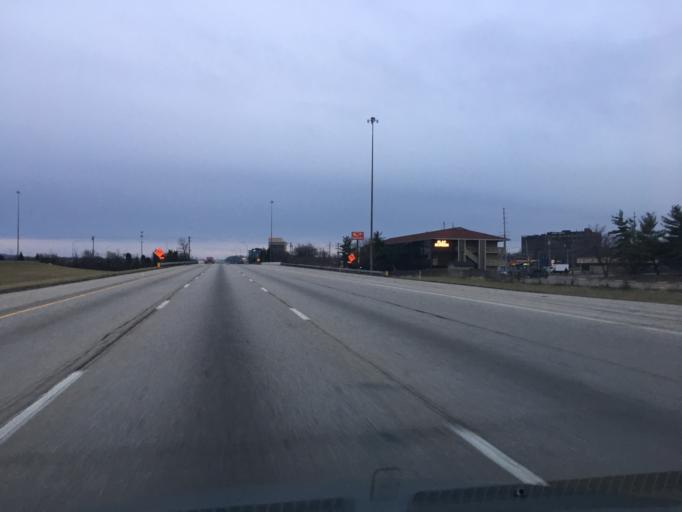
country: US
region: Ohio
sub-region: Hamilton County
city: Glendale
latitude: 39.2875
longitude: -84.4419
